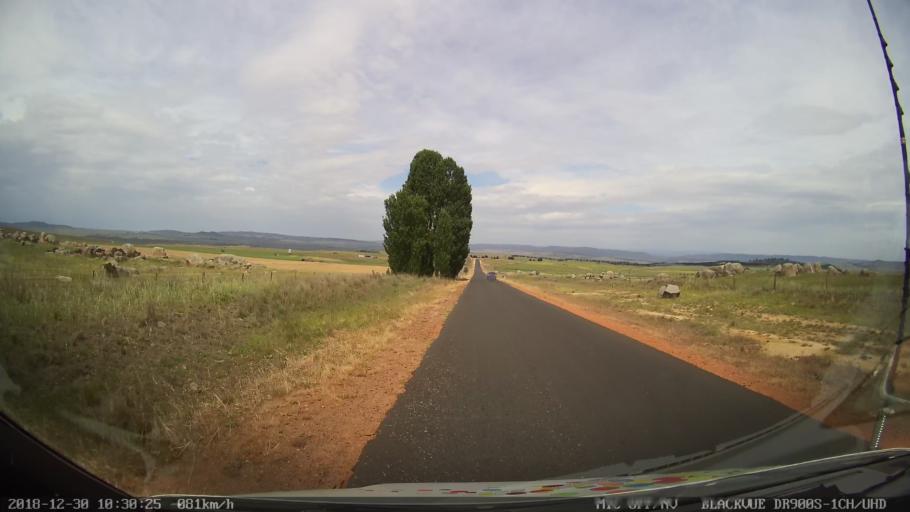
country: AU
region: New South Wales
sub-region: Snowy River
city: Berridale
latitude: -36.5037
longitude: 148.8954
